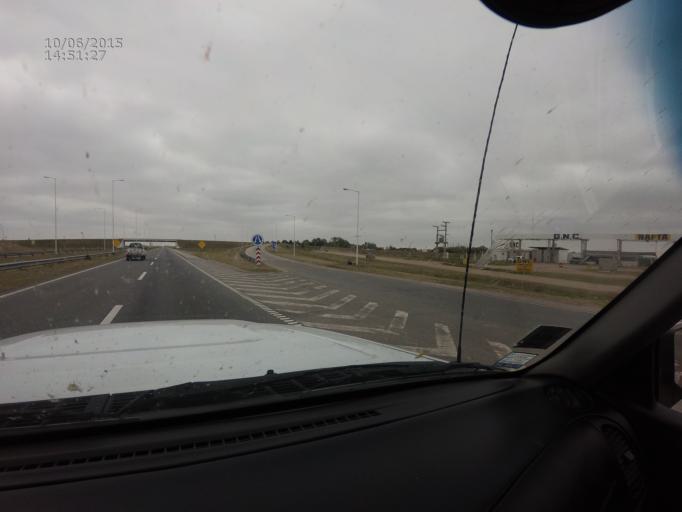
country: AR
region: Cordoba
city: Oncativo
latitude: -31.8979
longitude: -63.6447
